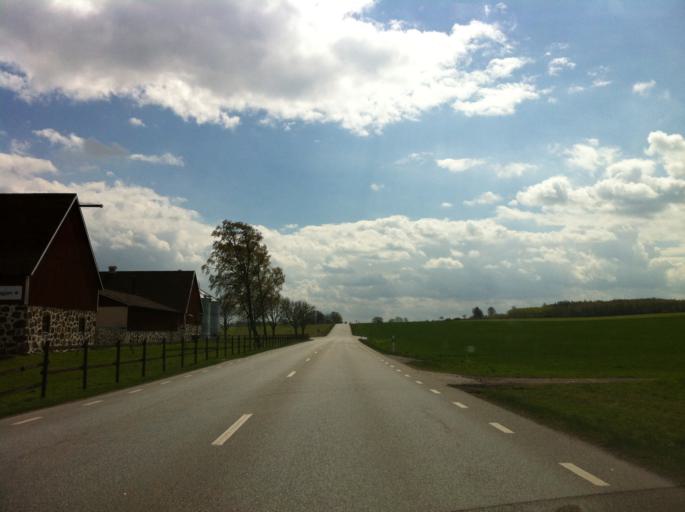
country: SE
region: Skane
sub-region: Hoors Kommun
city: Loberod
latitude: 55.8562
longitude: 13.4993
